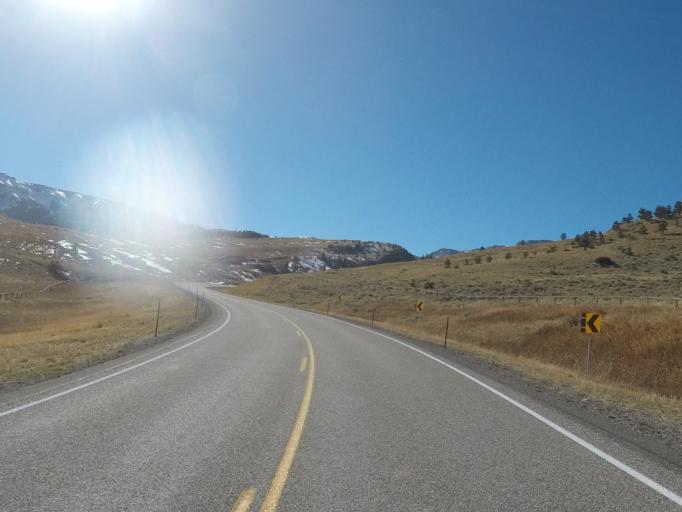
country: US
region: Wyoming
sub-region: Park County
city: Cody
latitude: 44.7138
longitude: -109.2900
